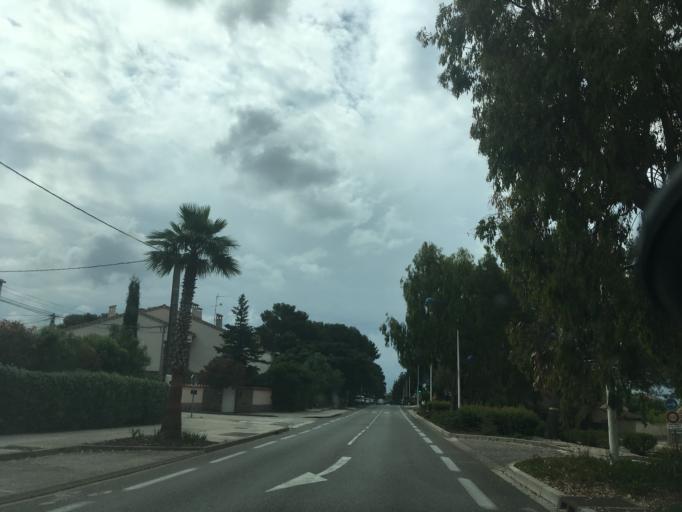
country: FR
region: Provence-Alpes-Cote d'Azur
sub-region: Departement du Var
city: La Londe-les-Maures
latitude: 43.1334
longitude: 6.2379
